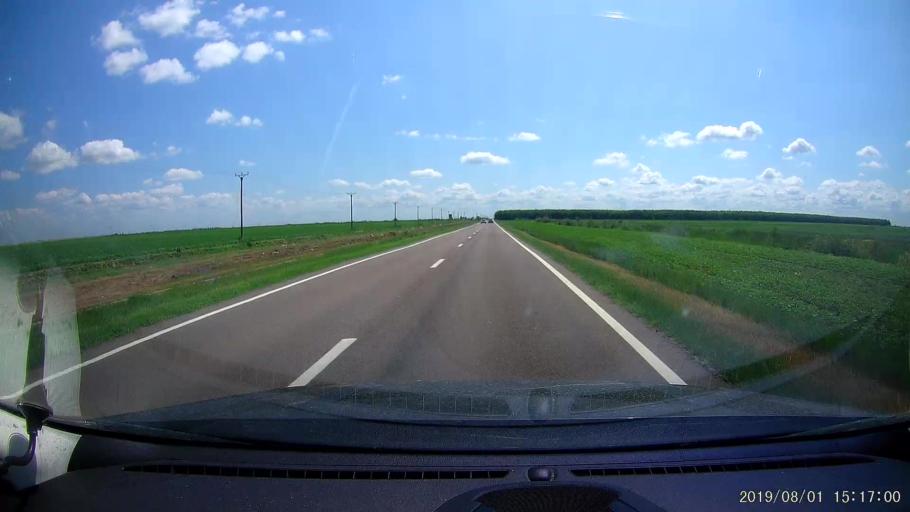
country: RO
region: Braila
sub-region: Comuna Unirea
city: Unirea
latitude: 45.1362
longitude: 27.8434
